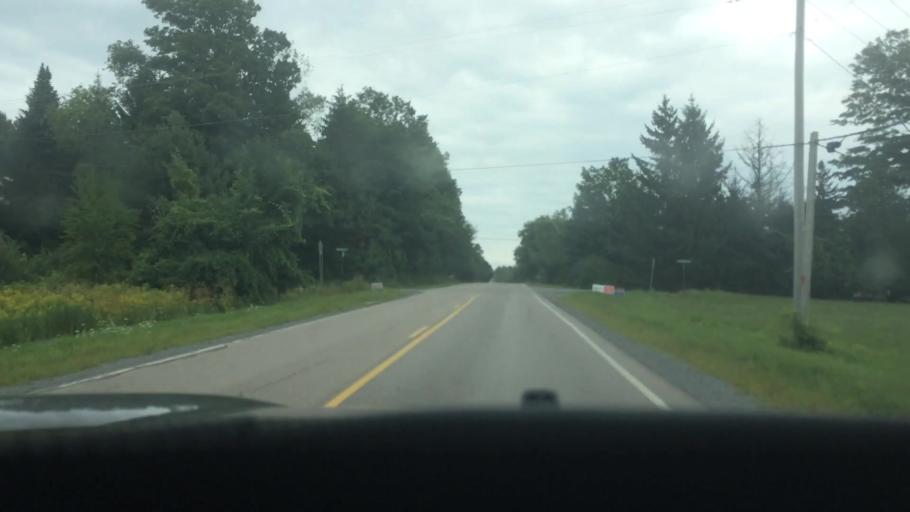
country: US
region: New York
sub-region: St. Lawrence County
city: Hannawa Falls
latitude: 44.5380
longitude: -75.0544
